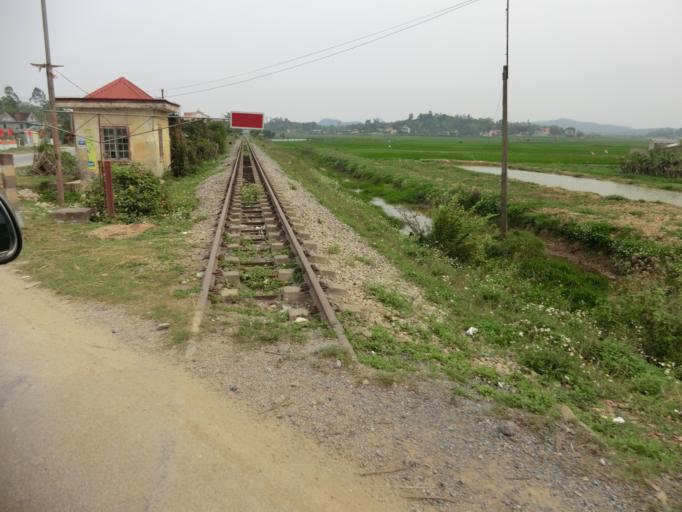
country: VN
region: Nghe An
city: Cau Giat
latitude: 19.2130
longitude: 105.5469
